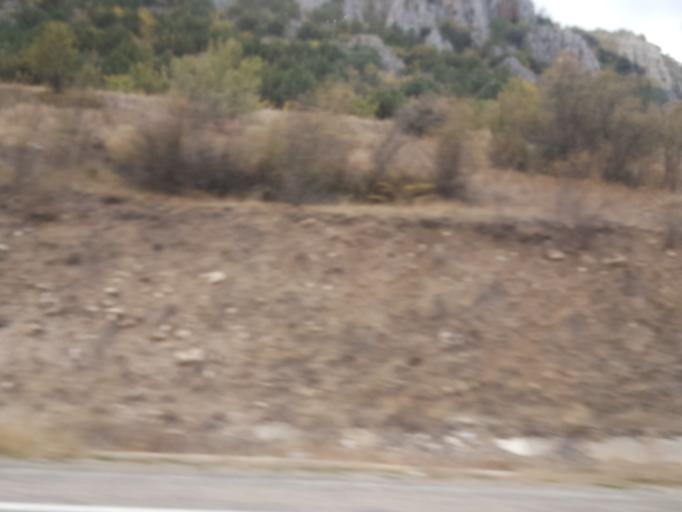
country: TR
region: Yozgat
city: Aydincik
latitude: 40.1854
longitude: 35.3938
